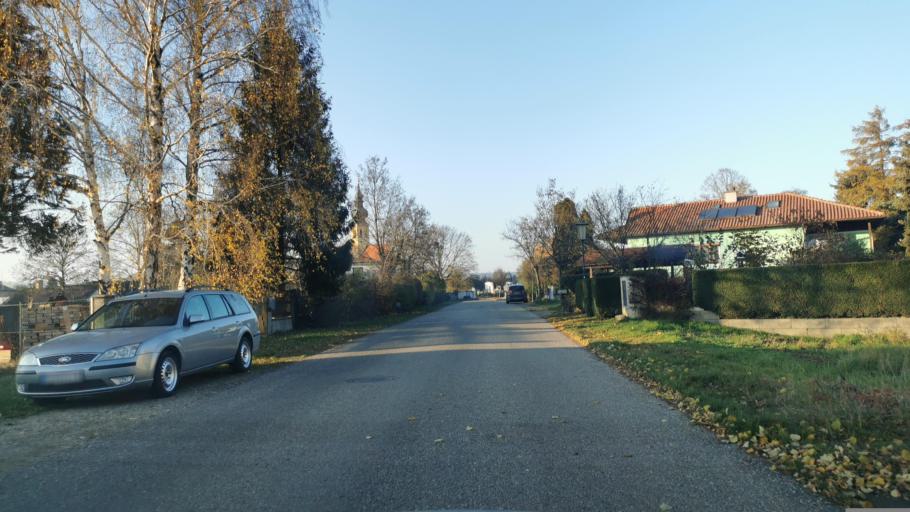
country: AT
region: Lower Austria
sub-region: Politischer Bezirk Korneuburg
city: Harmannsdorf
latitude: 48.3893
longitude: 16.3745
